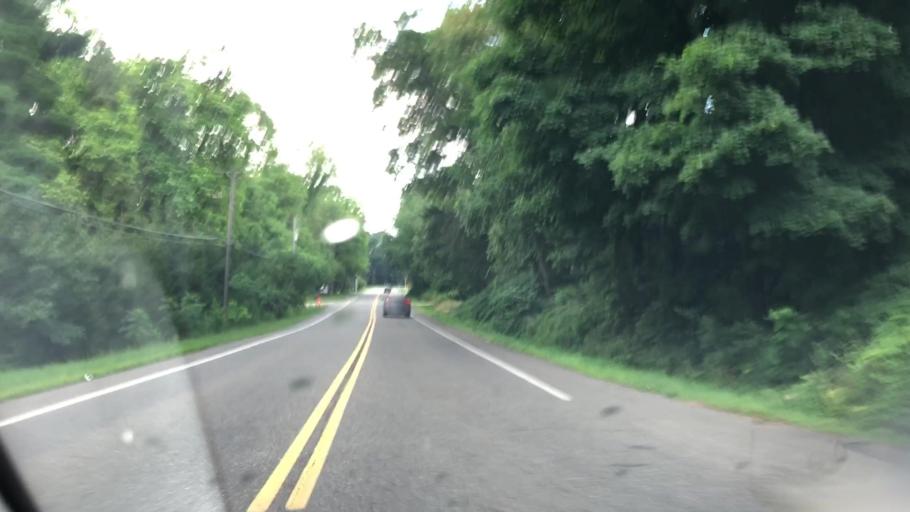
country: US
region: Ohio
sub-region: Summit County
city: Portage Lakes
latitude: 40.9872
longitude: -81.5481
